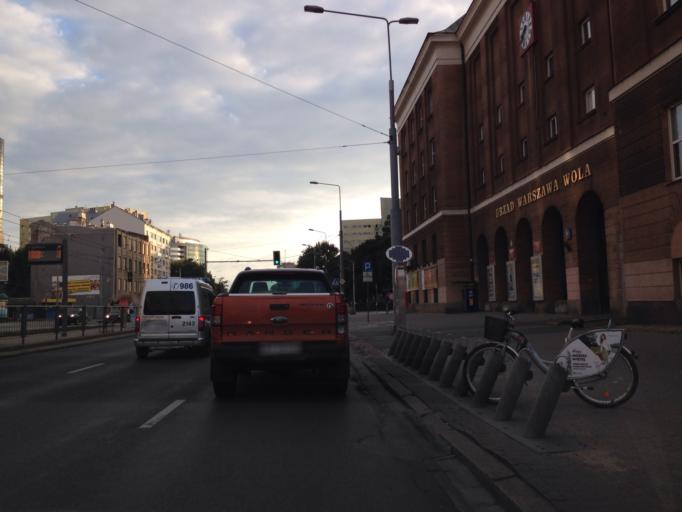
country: PL
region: Masovian Voivodeship
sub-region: Warszawa
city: Wola
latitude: 52.2403
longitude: 20.9884
